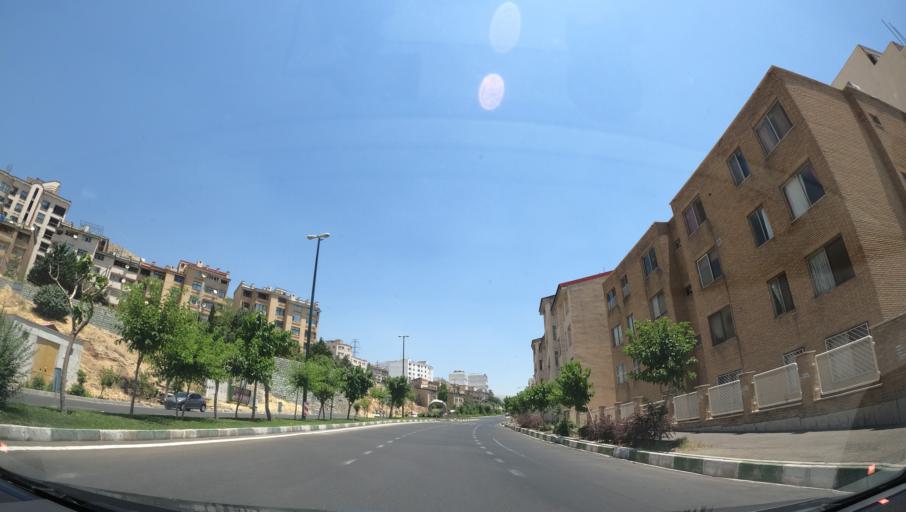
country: IR
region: Tehran
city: Tajrish
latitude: 35.8103
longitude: 51.3907
